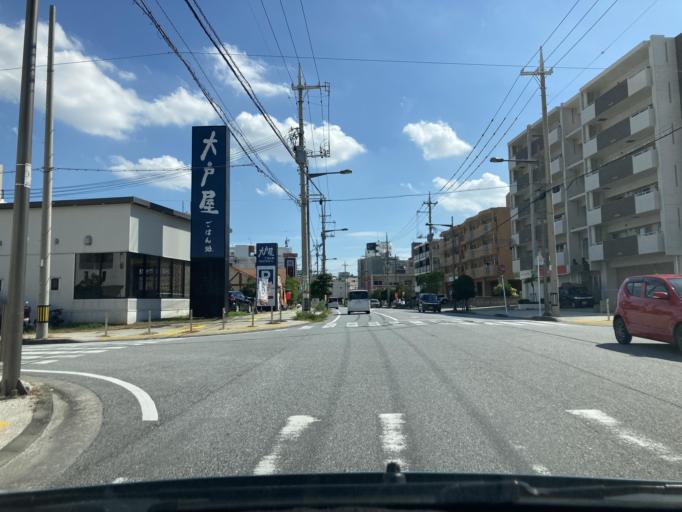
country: JP
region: Okinawa
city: Ginowan
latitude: 26.2712
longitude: 127.7311
